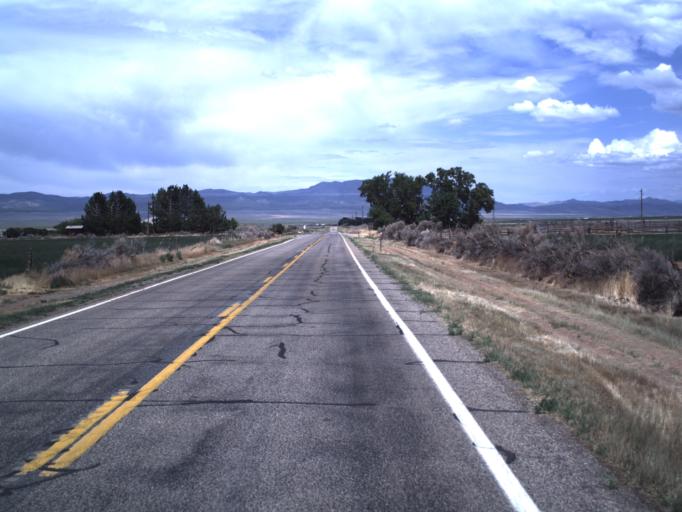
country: US
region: Utah
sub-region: Iron County
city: Parowan
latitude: 37.8949
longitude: -112.7748
